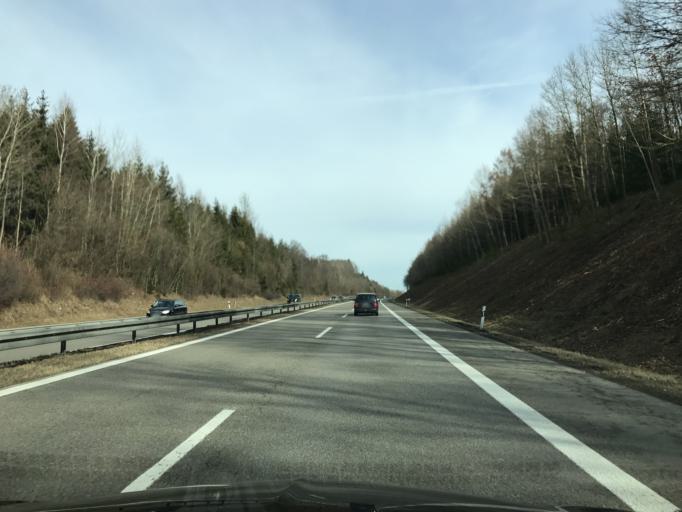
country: DE
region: Bavaria
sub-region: Swabia
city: Buxheim
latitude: 47.9818
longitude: 10.1265
